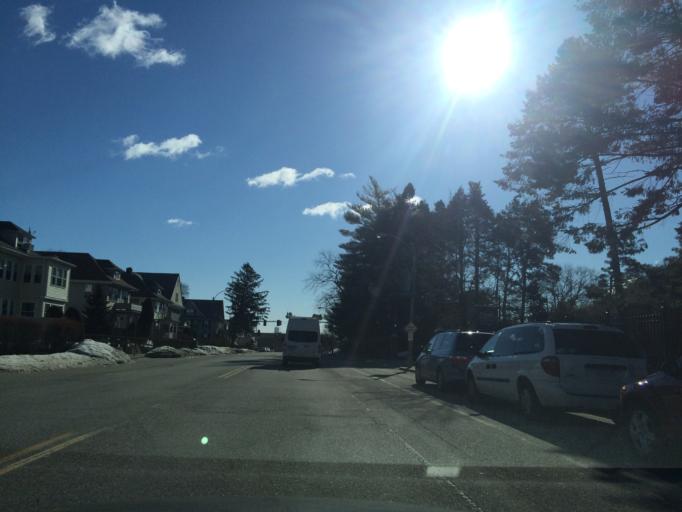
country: US
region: Massachusetts
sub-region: Middlesex County
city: Watertown
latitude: 42.3635
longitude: -71.1750
